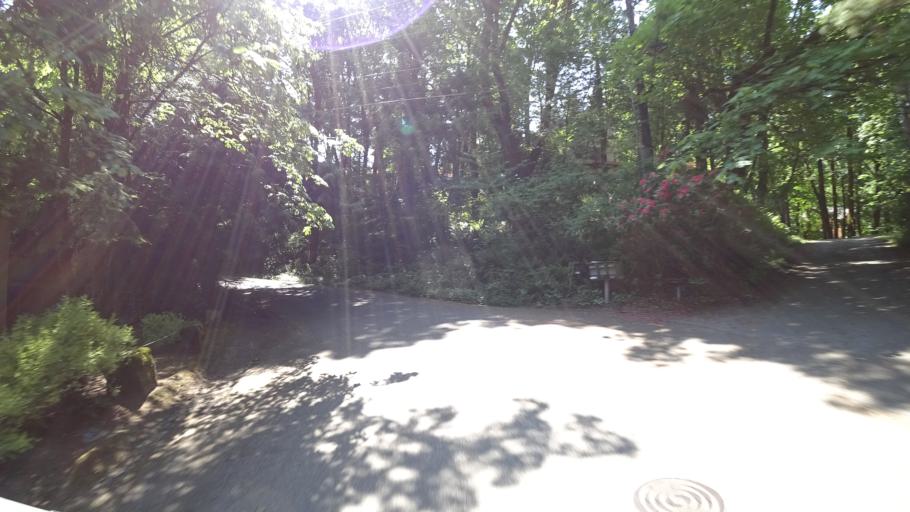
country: US
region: Oregon
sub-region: Washington County
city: West Haven-Sylvan
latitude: 45.5194
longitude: -122.7286
